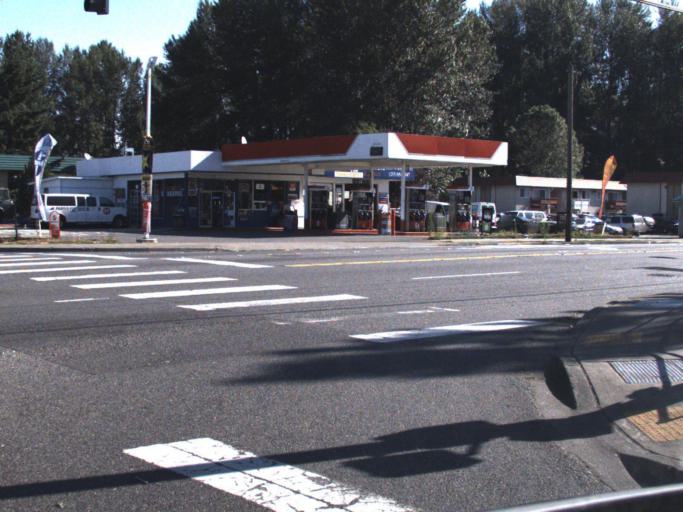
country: US
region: Washington
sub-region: King County
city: Kent
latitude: 47.3866
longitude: -122.2474
